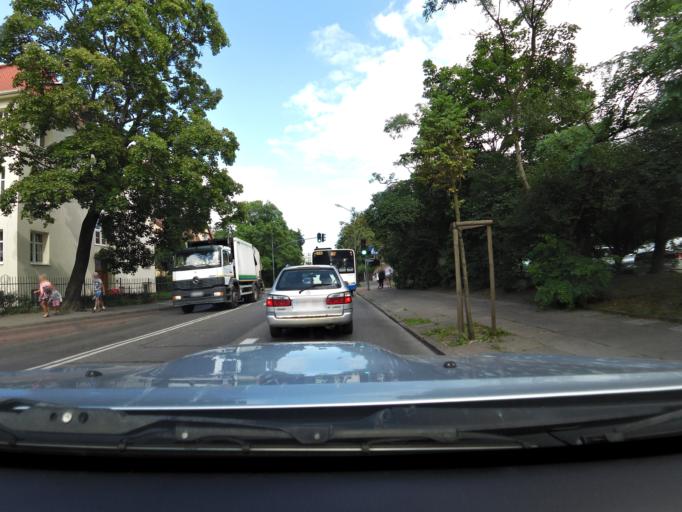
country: PL
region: Pomeranian Voivodeship
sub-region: Sopot
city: Sopot
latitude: 54.4360
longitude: 18.5677
